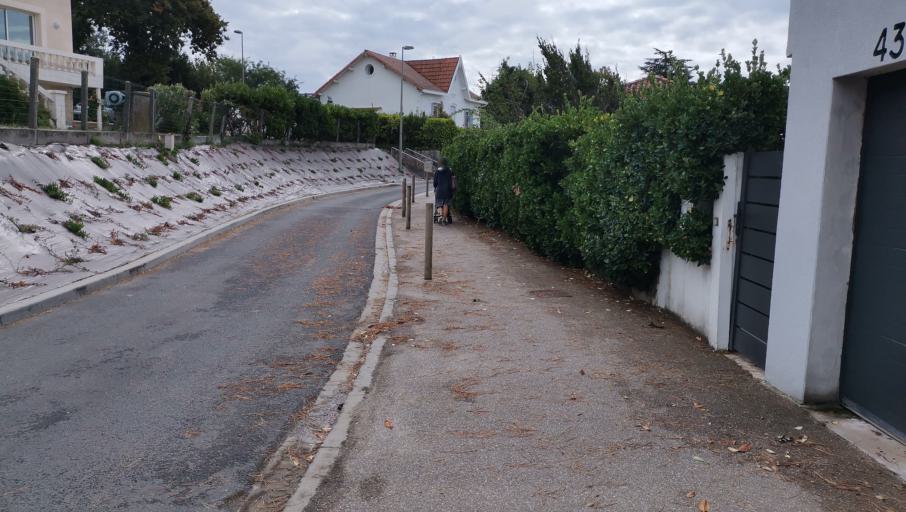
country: FR
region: Poitou-Charentes
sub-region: Departement de la Charente-Maritime
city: Meschers-sur-Gironde
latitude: 45.5588
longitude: -0.9632
